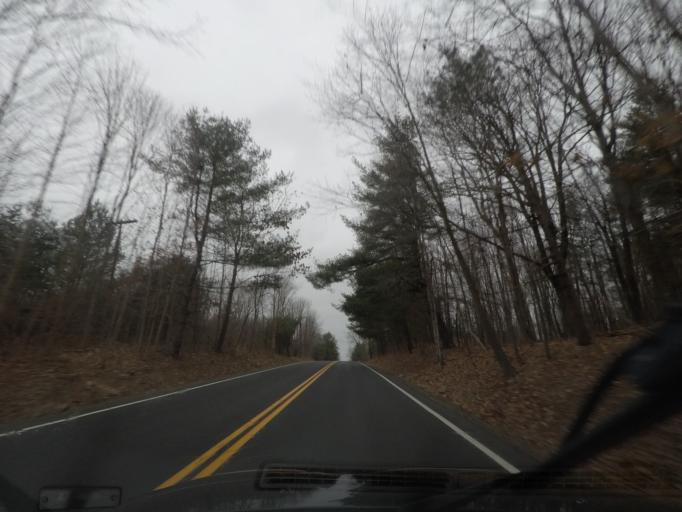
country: US
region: New York
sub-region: Rensselaer County
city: East Greenbush
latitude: 42.6061
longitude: -73.6562
